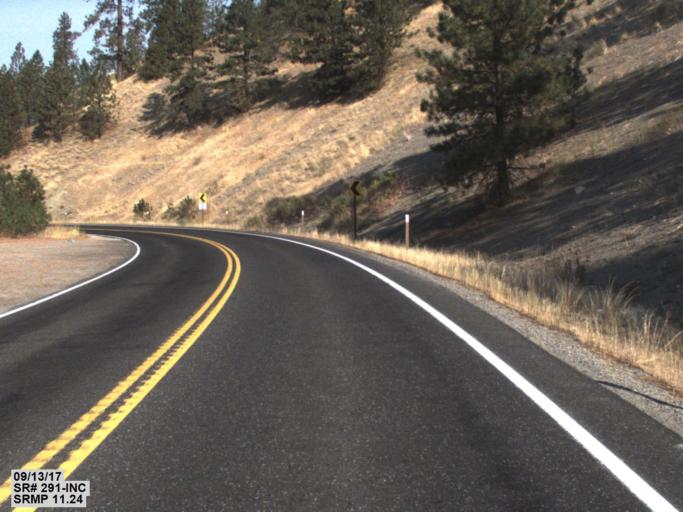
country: US
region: Washington
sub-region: Spokane County
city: Fairwood
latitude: 47.7979
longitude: -117.5354
